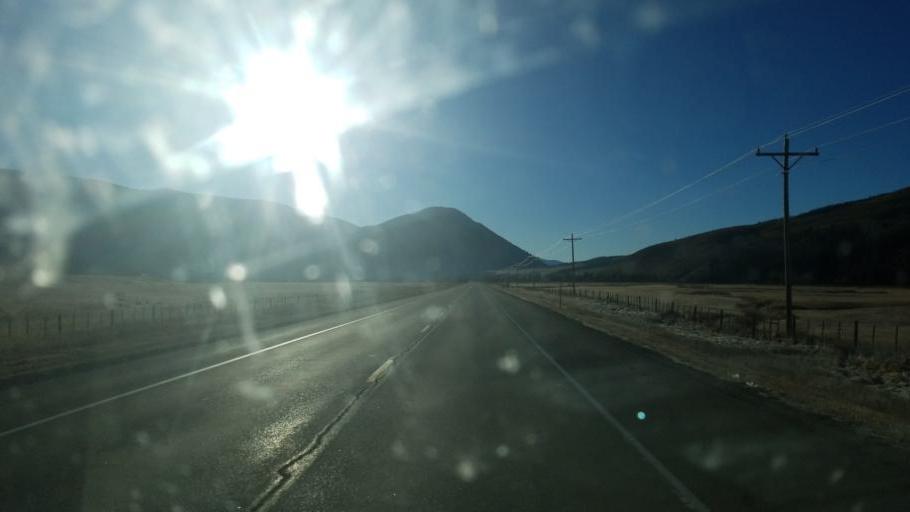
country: US
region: Colorado
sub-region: Gunnison County
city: Crested Butte
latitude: 38.8224
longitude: -106.9150
